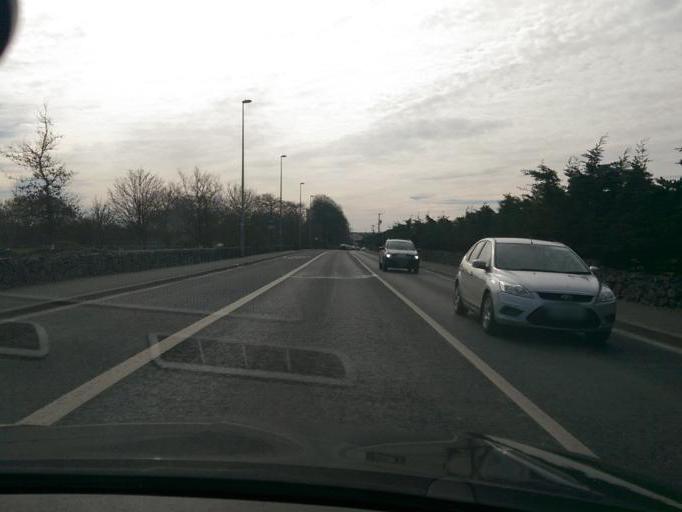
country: IE
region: Connaught
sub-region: County Galway
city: Claregalway
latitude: 53.3495
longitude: -8.9392
